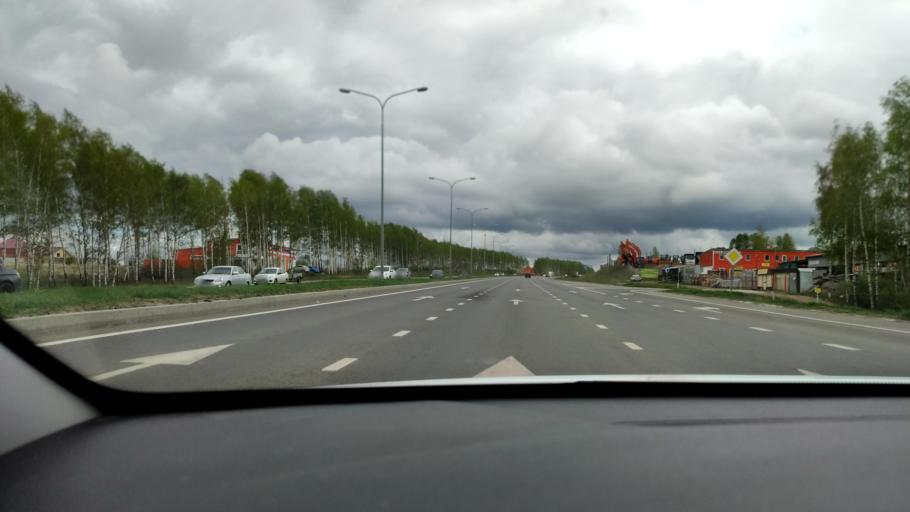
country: RU
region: Tatarstan
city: Vysokaya Gora
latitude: 55.8018
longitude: 49.2831
